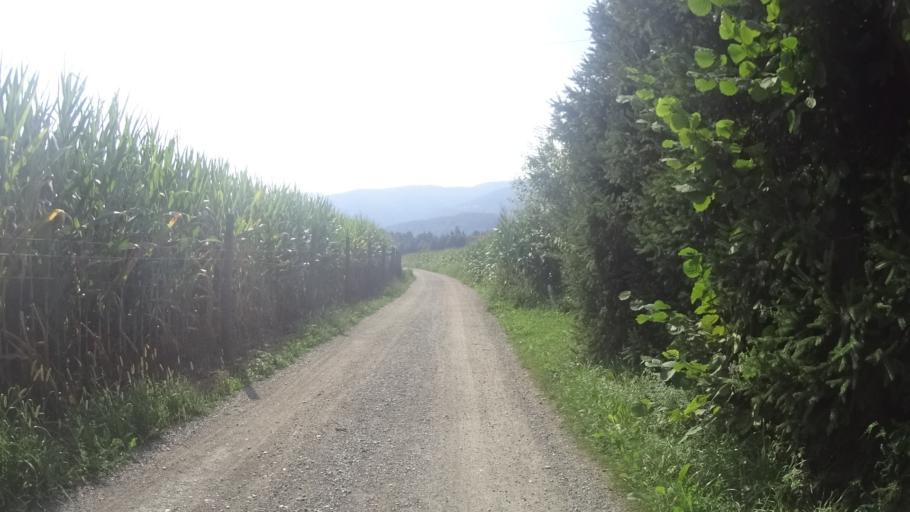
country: SI
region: Selnica ob Dravi
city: Selnica ob Dravi
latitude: 46.5452
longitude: 15.4740
